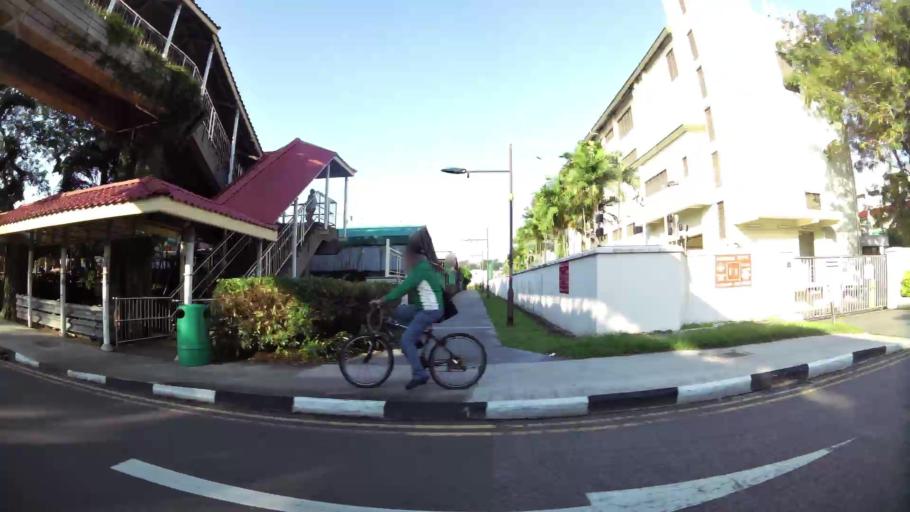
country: SG
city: Singapore
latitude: 1.3216
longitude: 103.9276
